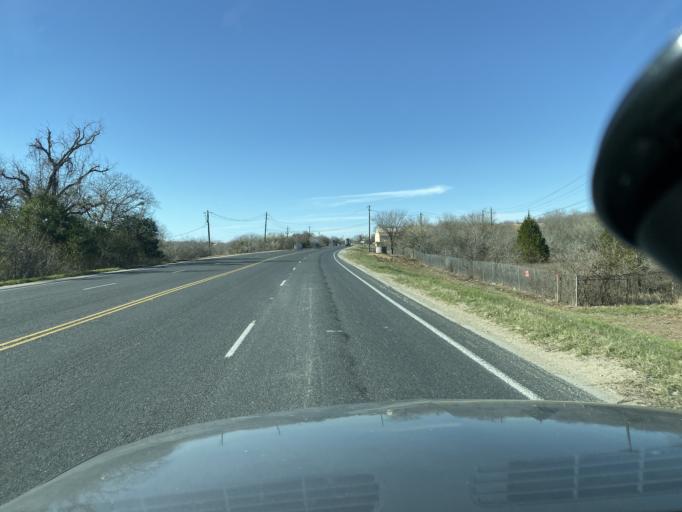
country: US
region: Texas
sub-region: Travis County
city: Garfield
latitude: 30.1709
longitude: -97.6649
